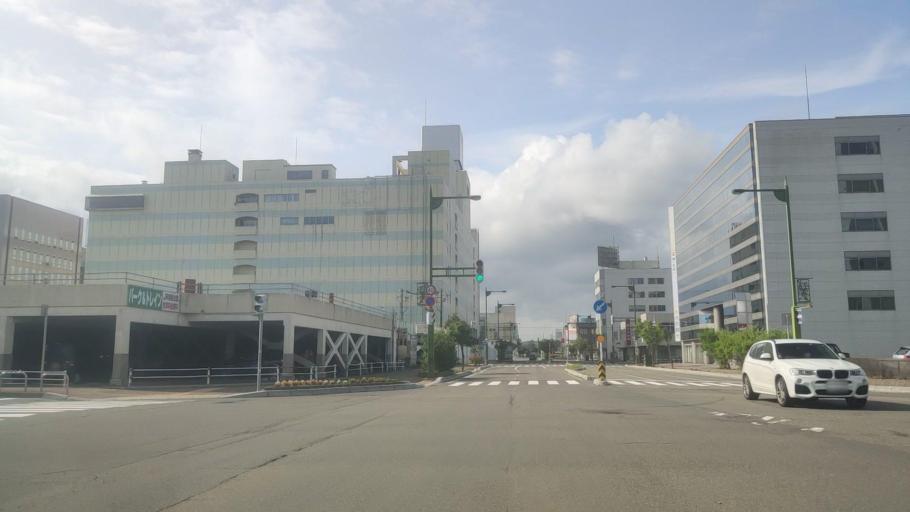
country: JP
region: Hokkaido
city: Tomakomai
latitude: 42.6374
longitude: 141.5988
